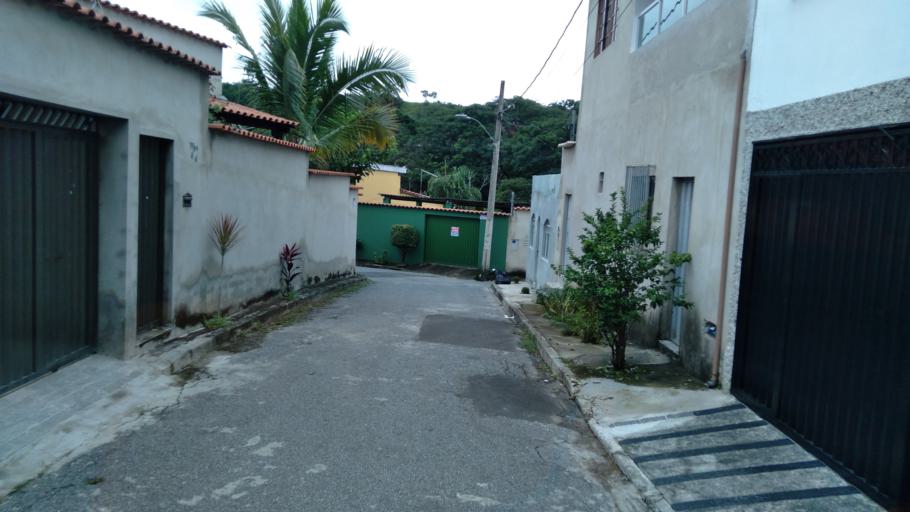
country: BR
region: Minas Gerais
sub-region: Santa Luzia
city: Santa Luzia
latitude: -19.8332
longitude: -43.8702
